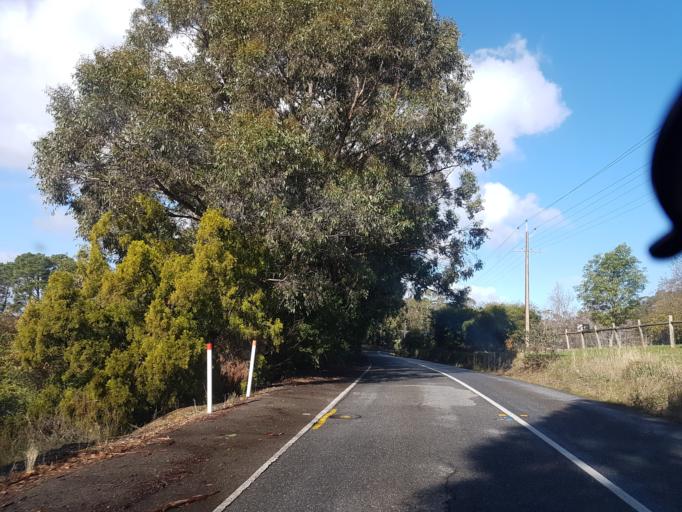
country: AU
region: South Australia
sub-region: Adelaide Hills
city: Heathfield
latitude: -35.0271
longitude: 138.7145
